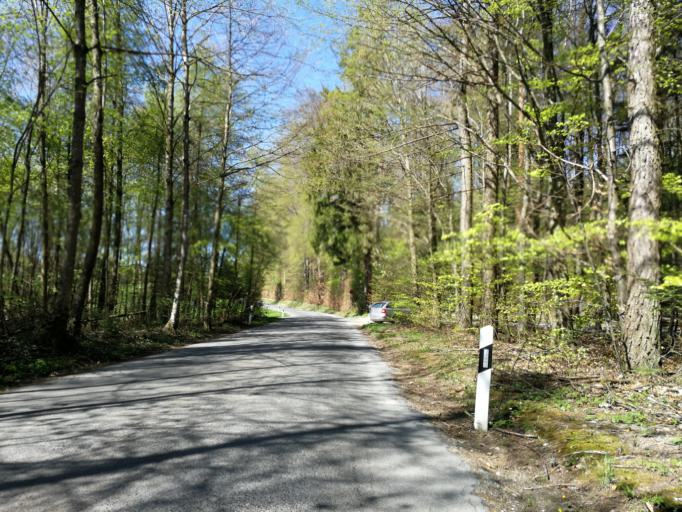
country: CH
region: Zurich
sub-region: Bezirk Uster
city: Aesch
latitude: 47.3101
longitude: 8.6610
